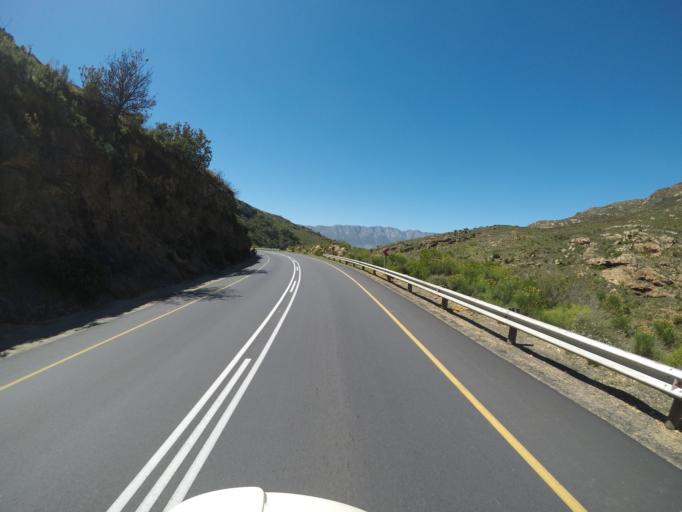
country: ZA
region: Western Cape
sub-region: Cape Winelands District Municipality
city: Ceres
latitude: -33.3184
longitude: 19.0825
